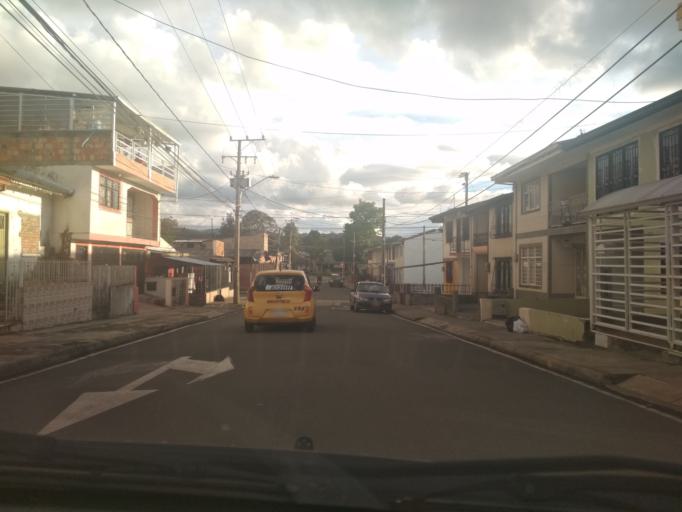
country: CO
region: Cauca
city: Popayan
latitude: 2.4369
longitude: -76.6126
